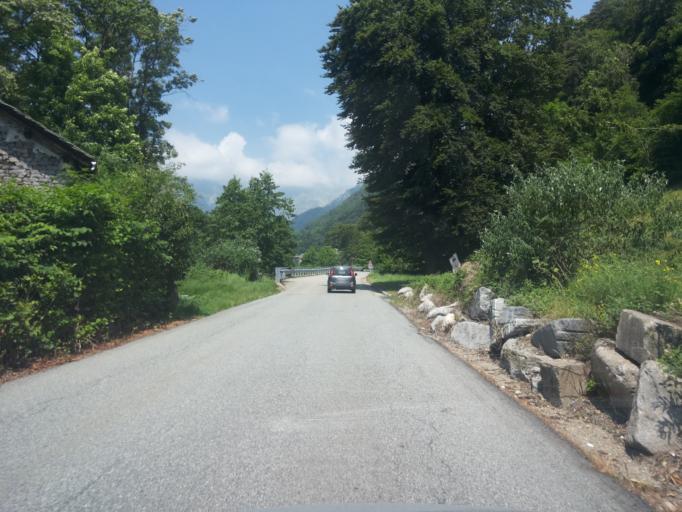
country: IT
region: Piedmont
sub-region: Provincia di Biella
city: Campiglia Cervo
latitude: 45.6669
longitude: 7.9931
